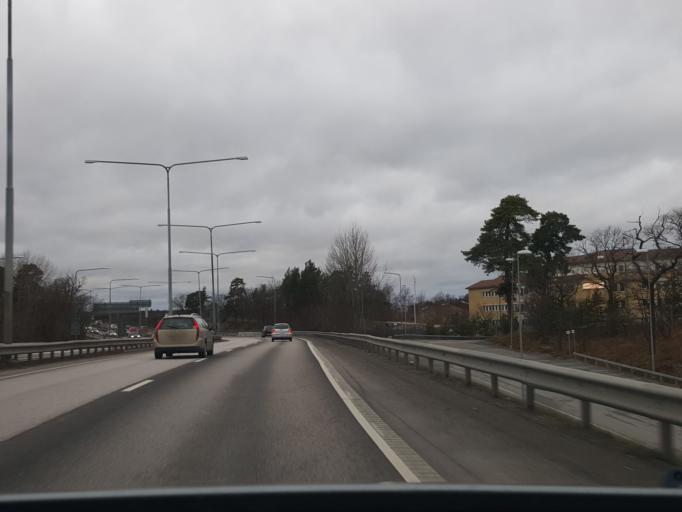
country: SE
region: Stockholm
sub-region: Lidingo
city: Brevik
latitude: 59.3139
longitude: 18.2285
